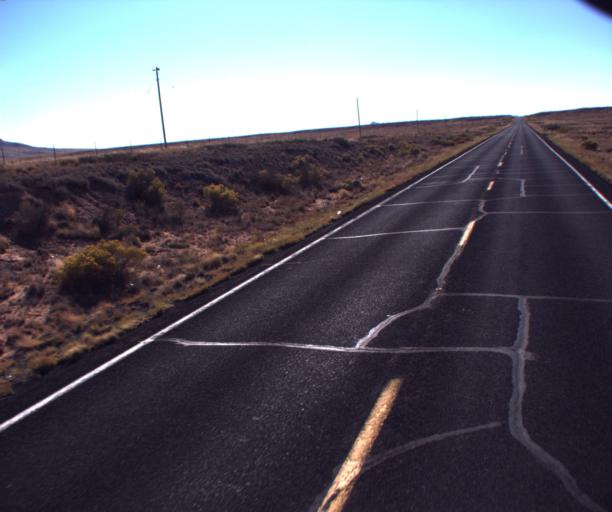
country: US
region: Arizona
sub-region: Navajo County
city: Dilkon
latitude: 35.5619
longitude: -110.4570
